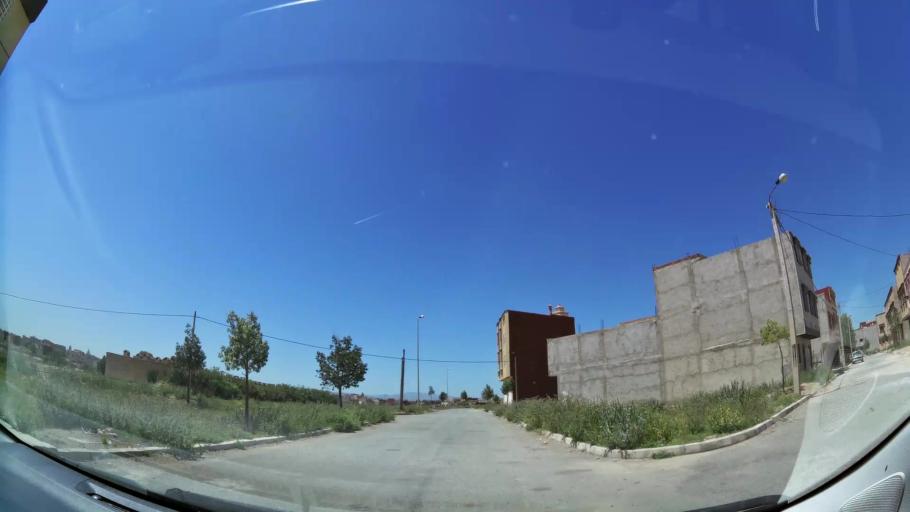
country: MA
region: Oriental
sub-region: Oujda-Angad
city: Oujda
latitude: 34.6721
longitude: -1.8609
